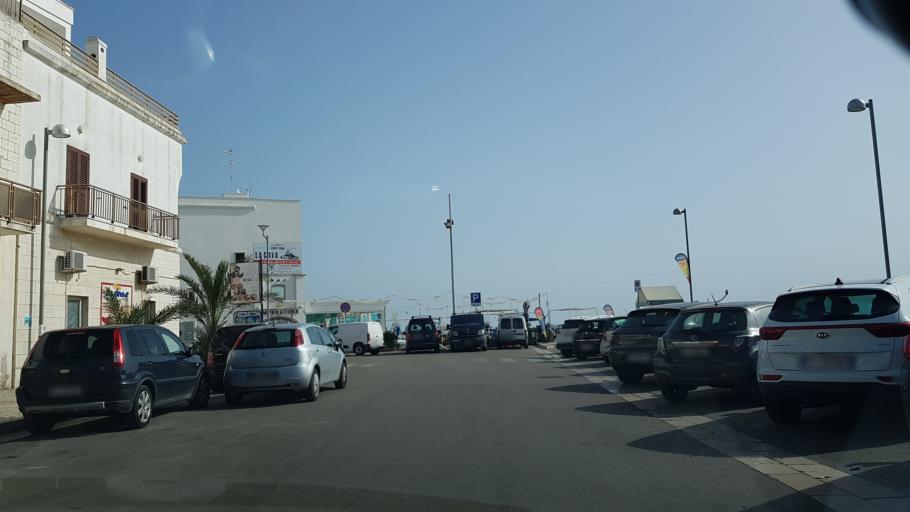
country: IT
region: Apulia
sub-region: Provincia di Lecce
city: Porto Cesareo
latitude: 40.2578
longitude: 17.8911
